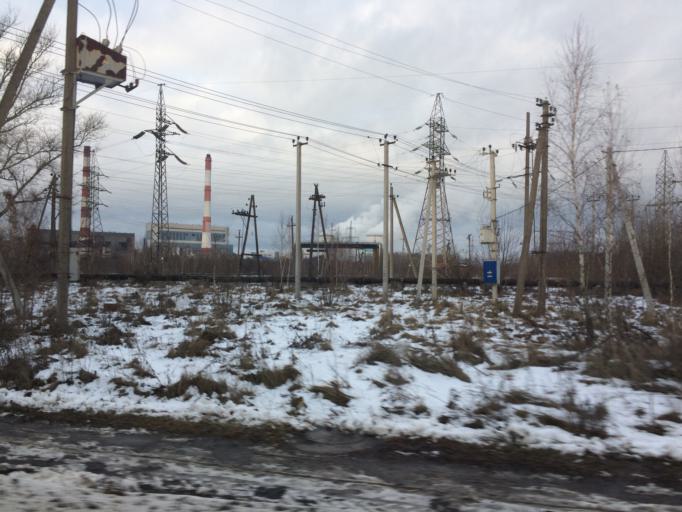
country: RU
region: Tula
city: Suvorov
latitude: 54.1276
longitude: 36.4818
